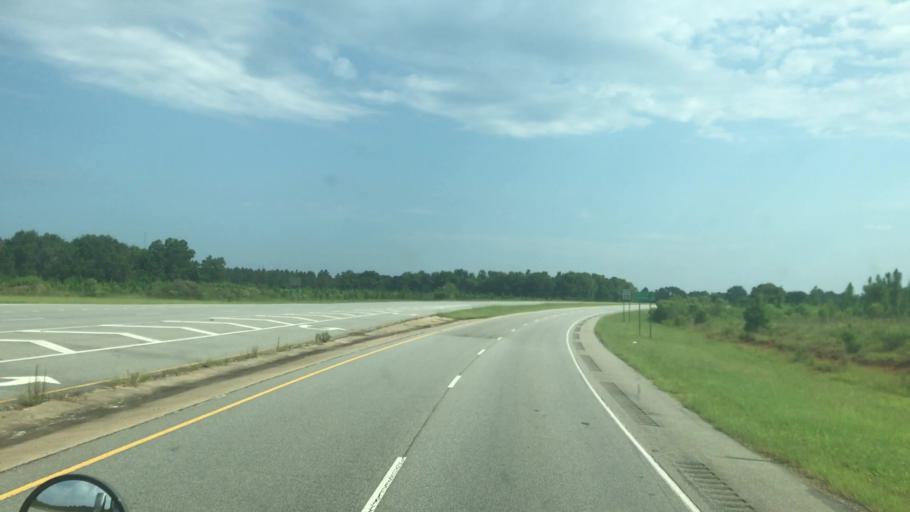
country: US
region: Georgia
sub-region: Early County
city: Blakely
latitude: 31.3589
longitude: -84.9233
